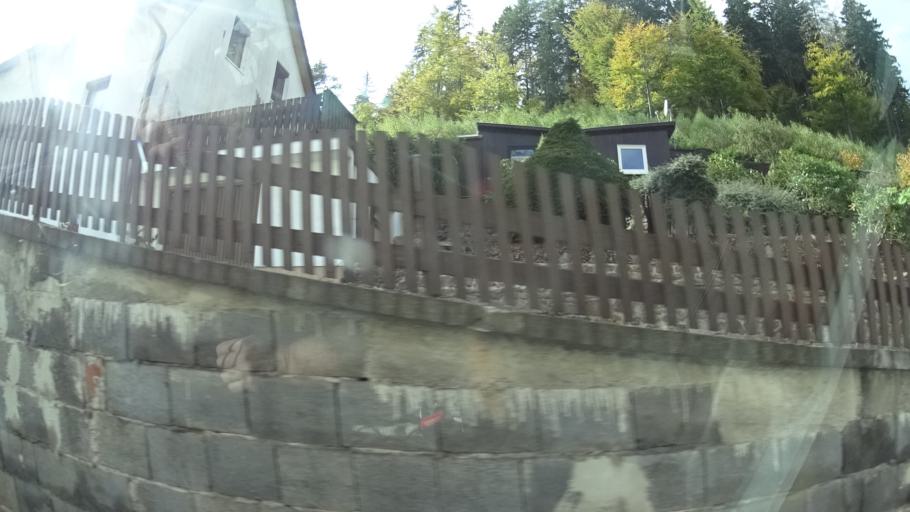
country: DE
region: Thuringia
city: Rotterode
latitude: 50.7079
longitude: 10.5630
